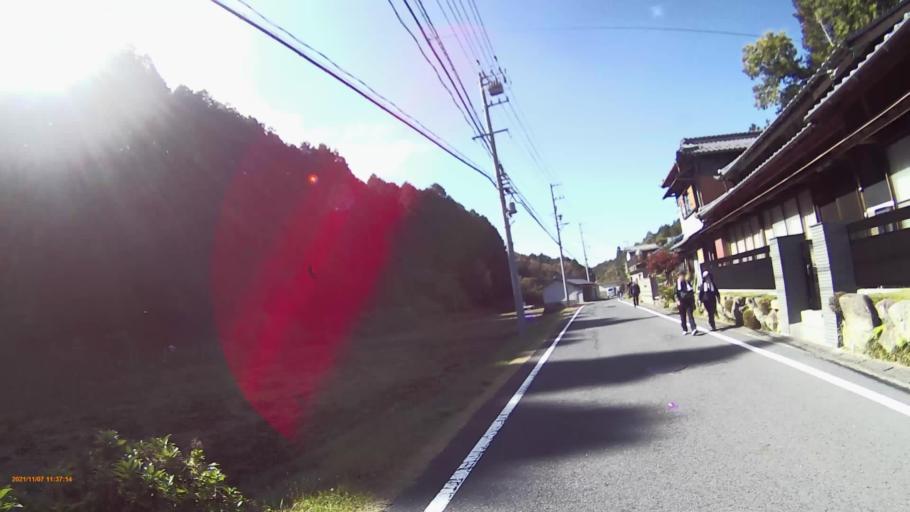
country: JP
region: Gifu
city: Mizunami
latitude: 35.4311
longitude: 137.2925
